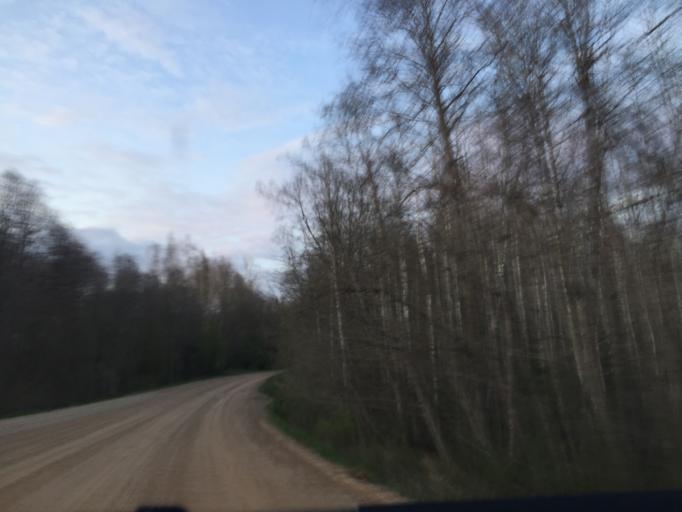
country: LV
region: Aluksnes Rajons
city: Aluksne
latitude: 57.3814
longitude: 27.0296
